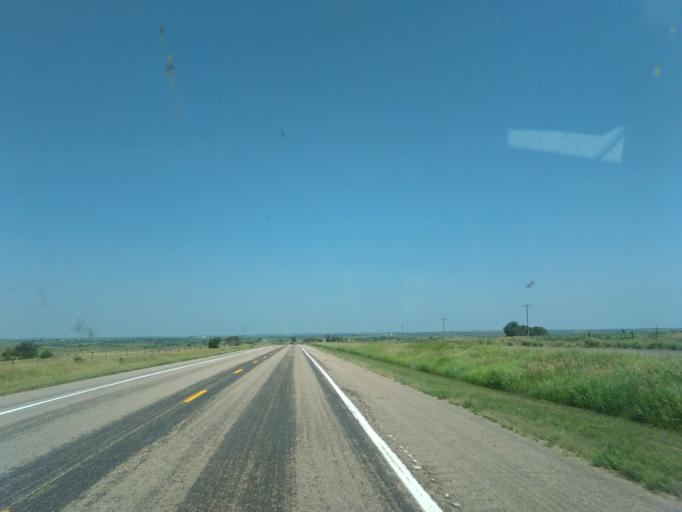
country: US
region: Nebraska
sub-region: Frontier County
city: Stockville
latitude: 40.6079
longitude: -100.6297
